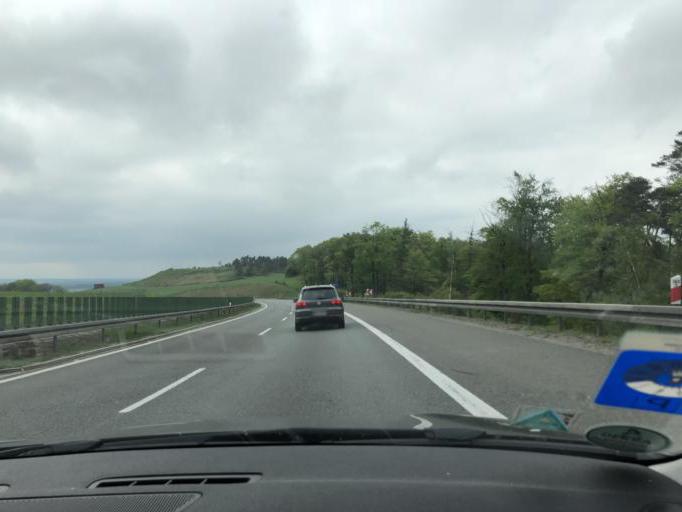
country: PL
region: Opole Voivodeship
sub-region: Powiat krapkowicki
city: Zdzieszowice
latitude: 50.4777
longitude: 18.1350
